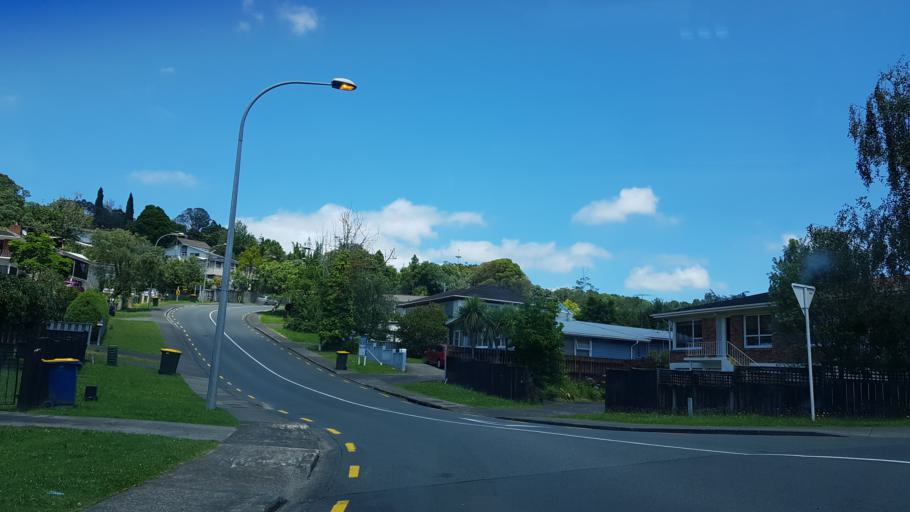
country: NZ
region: Auckland
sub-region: Auckland
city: North Shore
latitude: -36.7828
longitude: 174.7260
